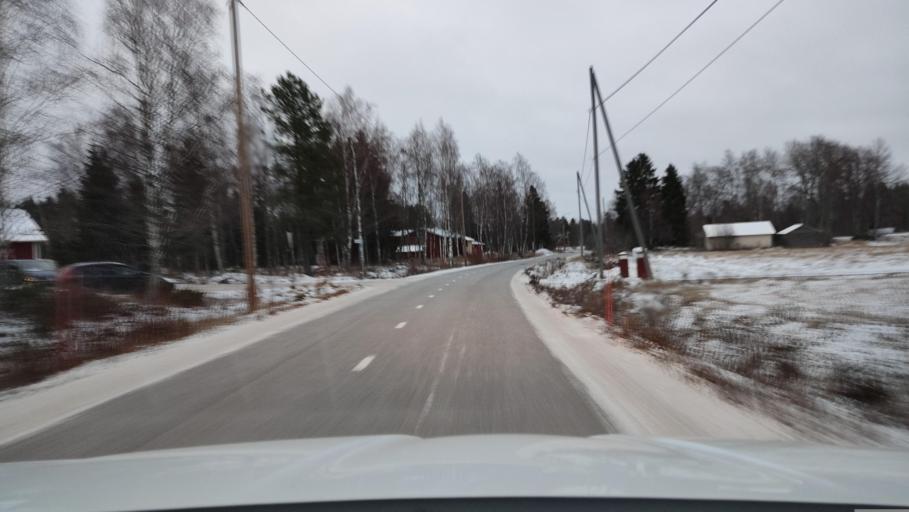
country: FI
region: Ostrobothnia
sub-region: Vaasa
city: Replot
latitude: 63.3466
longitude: 21.3091
